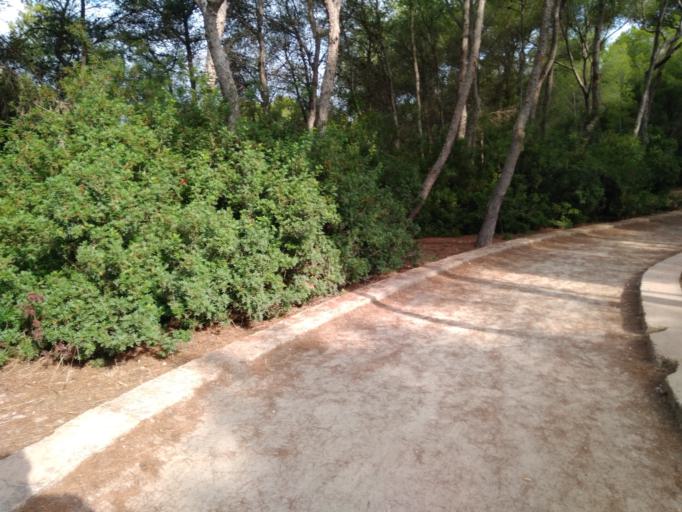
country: ES
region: Balearic Islands
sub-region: Illes Balears
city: s'Arenal
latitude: 39.5272
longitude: 2.7387
